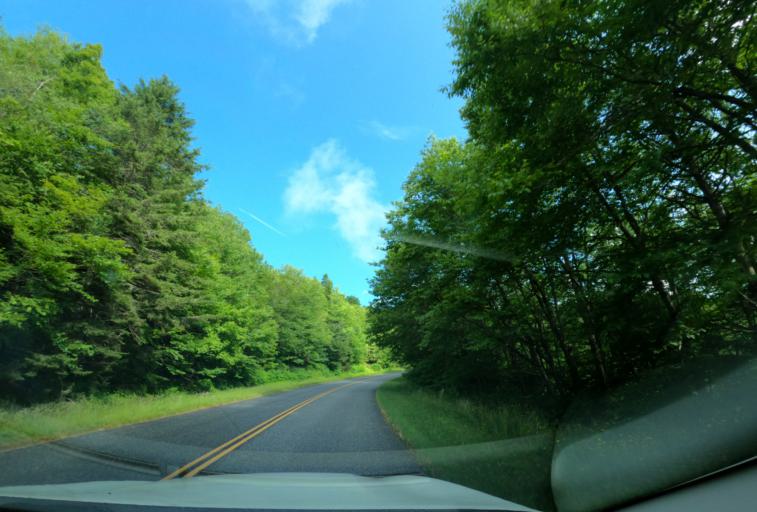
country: US
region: North Carolina
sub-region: Haywood County
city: Hazelwood
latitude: 35.3200
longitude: -82.9643
